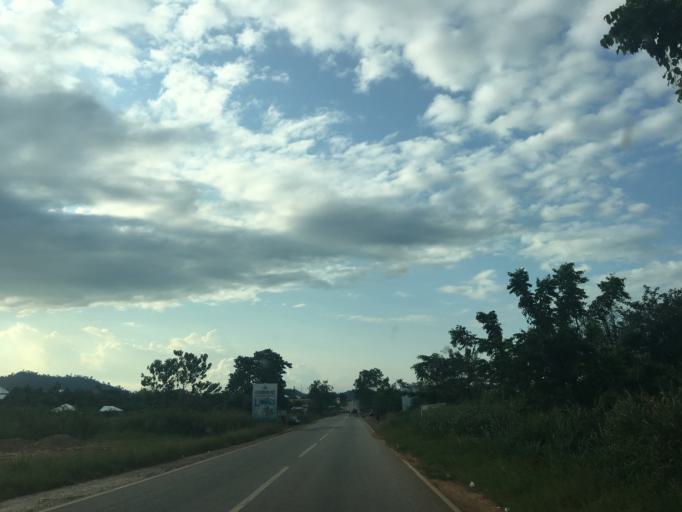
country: GH
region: Western
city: Bibiani
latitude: 6.4238
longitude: -2.3048
